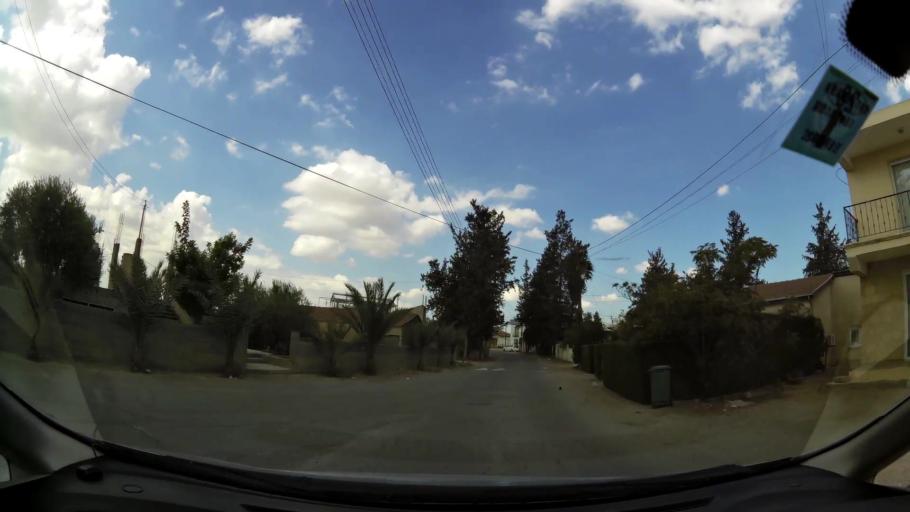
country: CY
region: Lefkosia
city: Nicosia
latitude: 35.2056
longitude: 33.3809
